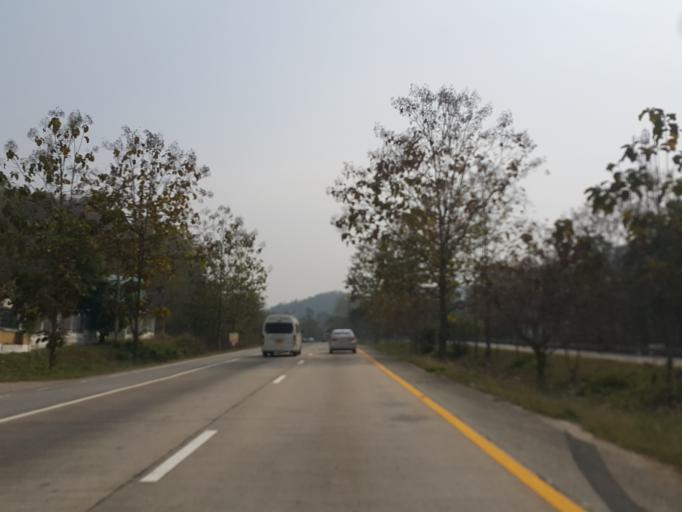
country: TH
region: Lamphun
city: Mae Tha
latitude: 18.5067
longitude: 99.1153
